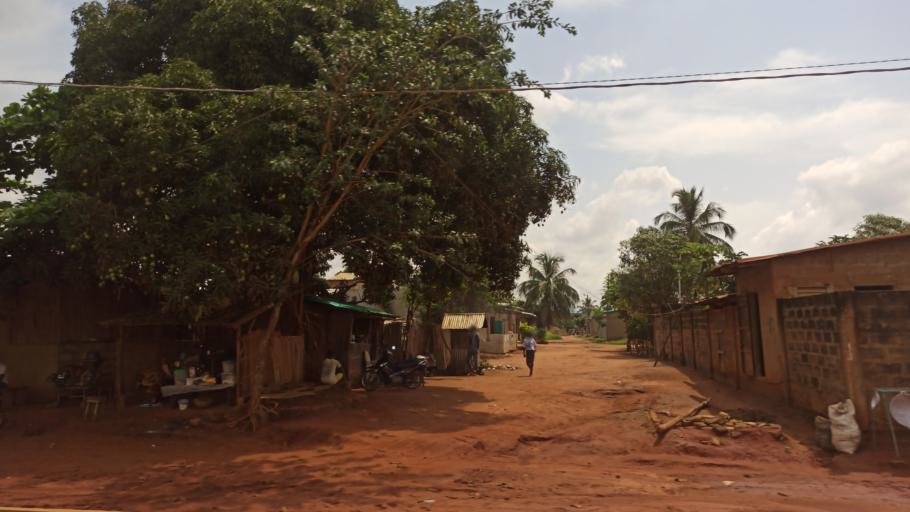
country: BJ
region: Queme
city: Porto-Novo
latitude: 6.4952
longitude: 2.5901
